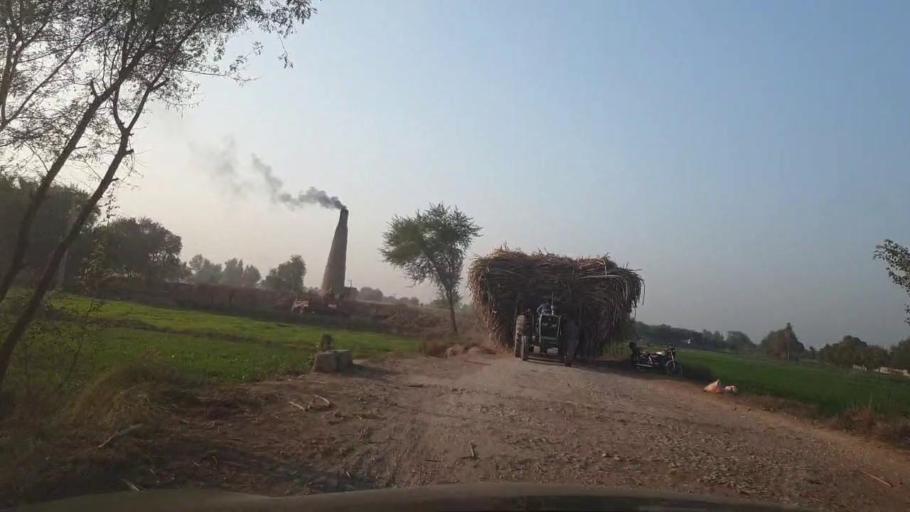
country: PK
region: Sindh
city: Ubauro
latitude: 28.3137
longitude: 69.7816
